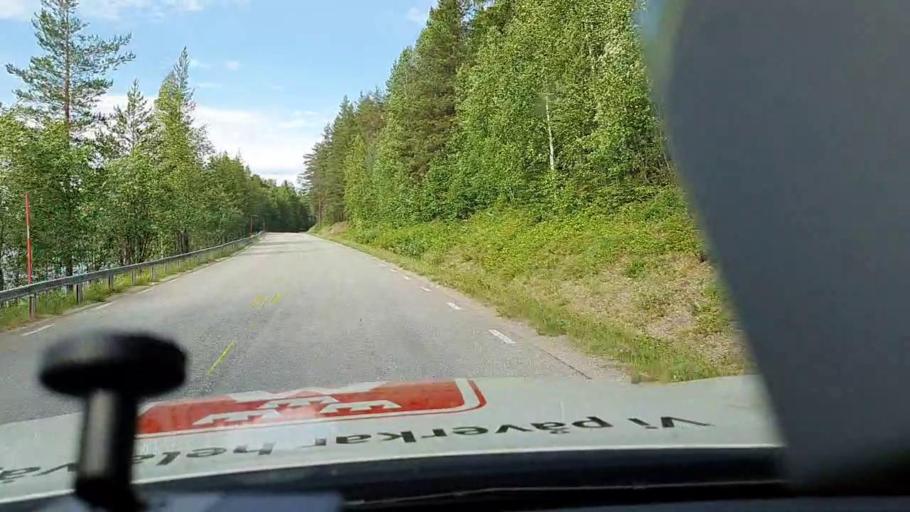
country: SE
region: Norrbotten
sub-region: Gallivare Kommun
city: Gaellivare
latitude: 66.4466
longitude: 20.6523
